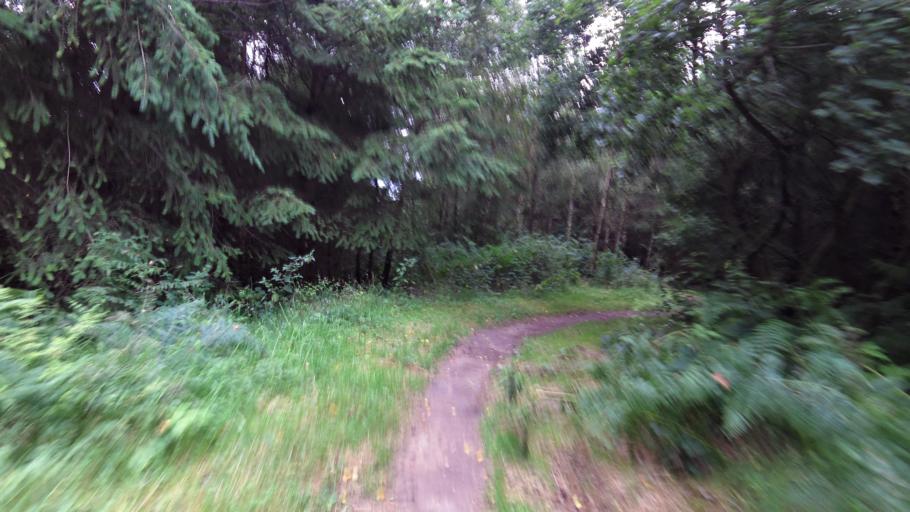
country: GB
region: England
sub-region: North Yorkshire
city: Thornton Dale
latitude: 54.2889
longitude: -0.6850
